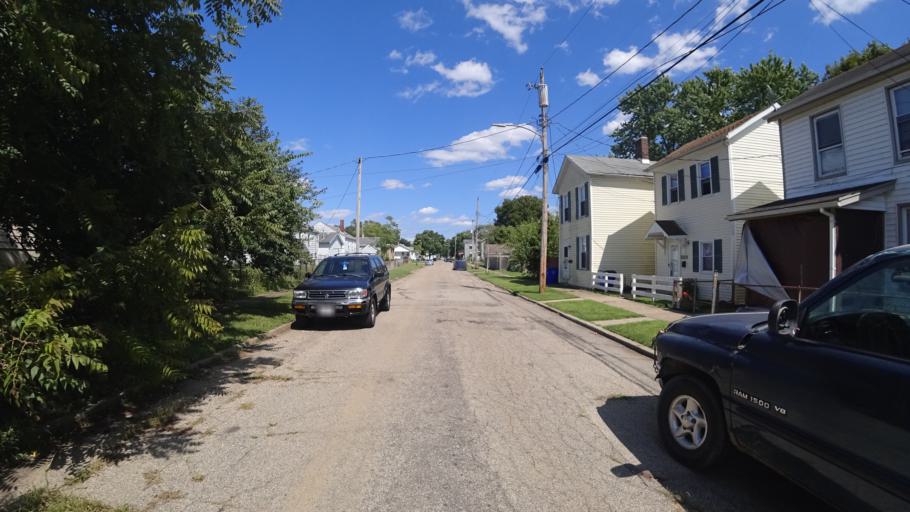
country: US
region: Ohio
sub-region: Butler County
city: Hamilton
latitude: 39.4047
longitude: -84.5496
